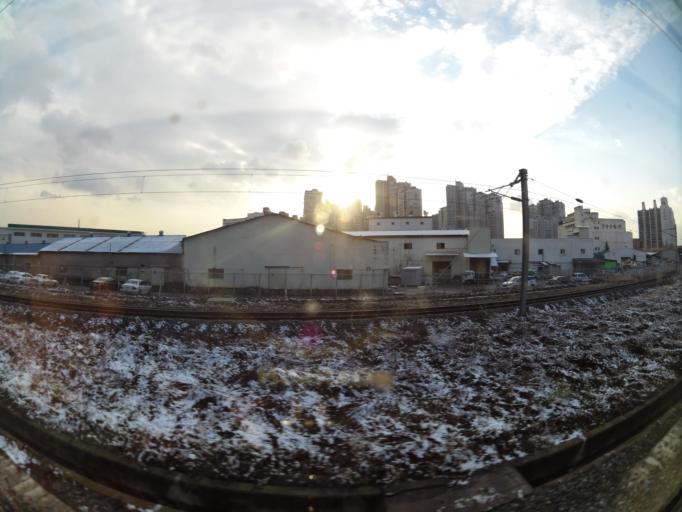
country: KR
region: Daejeon
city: Daejeon
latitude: 36.3420
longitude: 127.4283
